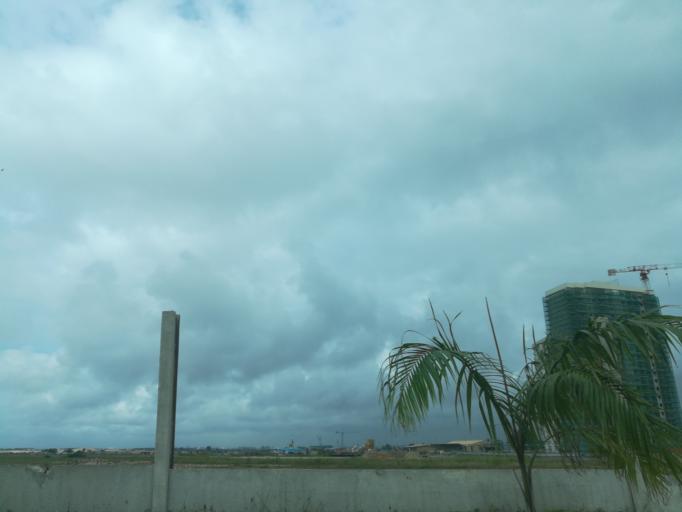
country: NG
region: Lagos
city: Lagos
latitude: 6.4172
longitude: 3.4127
